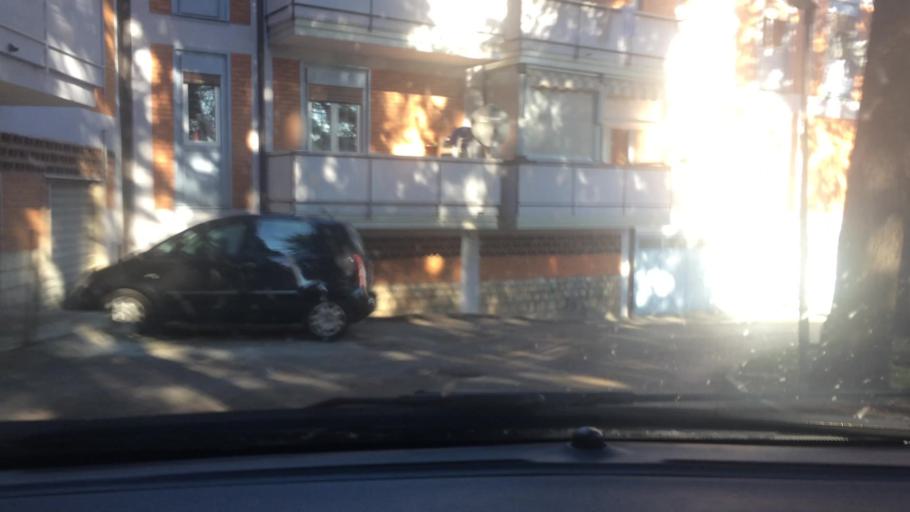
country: IT
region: Basilicate
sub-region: Provincia di Potenza
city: Potenza
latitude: 40.6486
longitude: 15.7950
